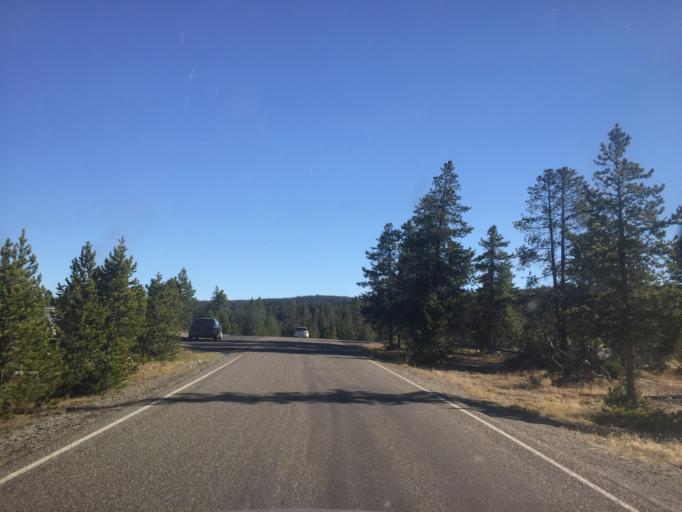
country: US
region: Montana
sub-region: Gallatin County
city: West Yellowstone
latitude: 44.5353
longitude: -110.8008
